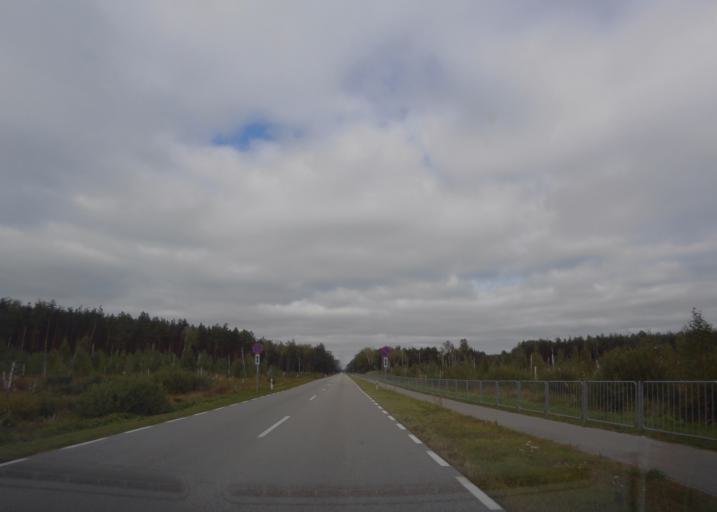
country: PL
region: Lublin Voivodeship
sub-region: Powiat wlodawski
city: Wlodawa
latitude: 51.4814
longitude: 23.5155
